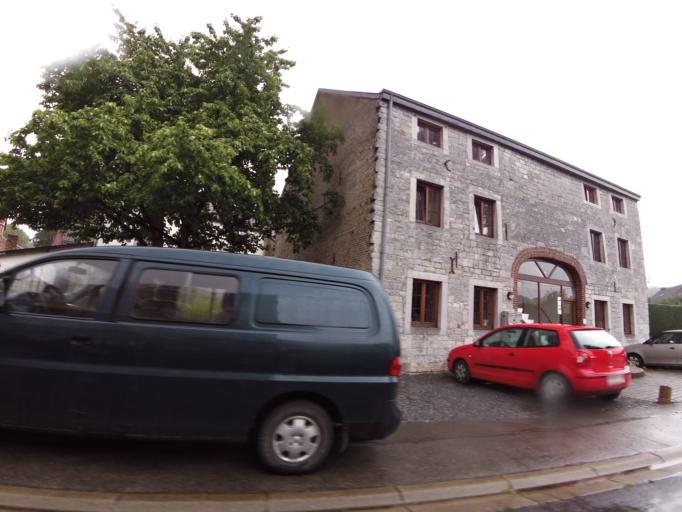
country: BE
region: Wallonia
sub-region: Province de Namur
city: Rochefort
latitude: 50.1614
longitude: 5.2263
